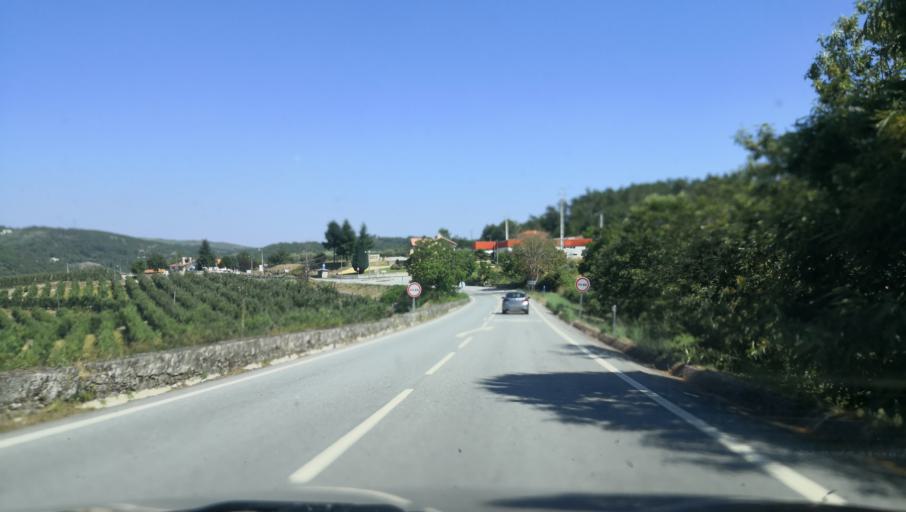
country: PT
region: Viseu
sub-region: Tarouca
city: Tarouca
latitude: 41.0274
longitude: -7.7162
